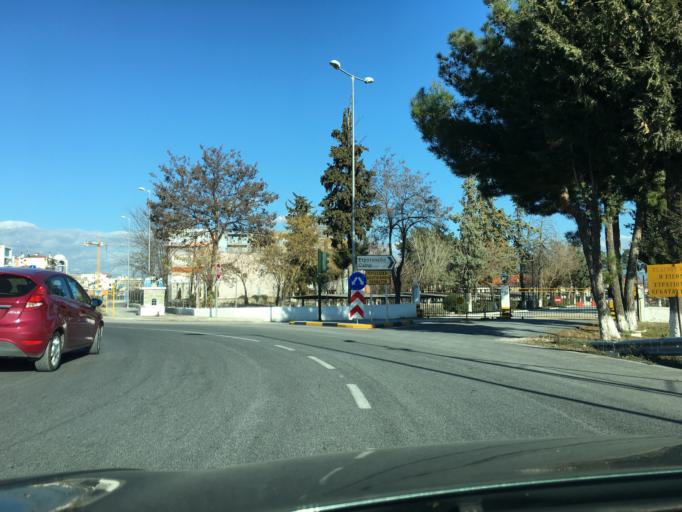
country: GR
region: Thessaly
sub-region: Nomos Larisis
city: Larisa
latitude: 39.6210
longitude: 22.4301
